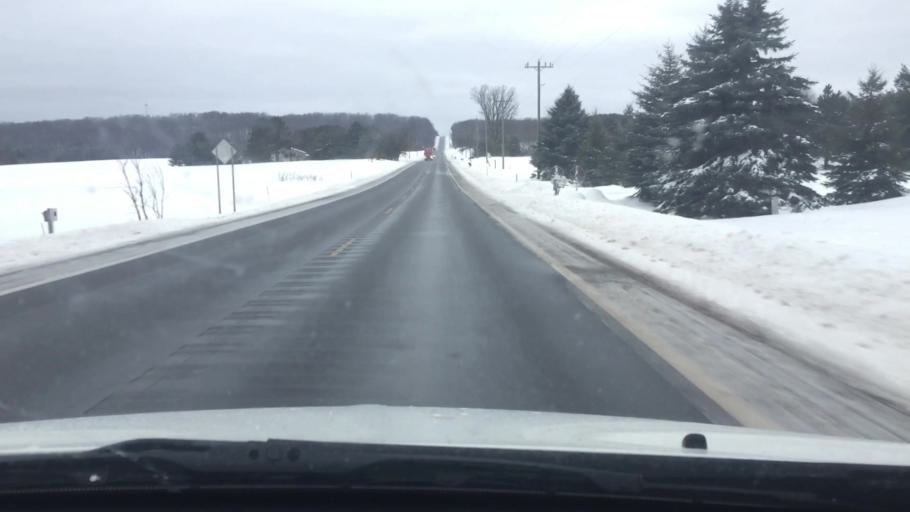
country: US
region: Michigan
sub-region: Charlevoix County
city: Boyne City
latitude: 45.0965
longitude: -84.9891
